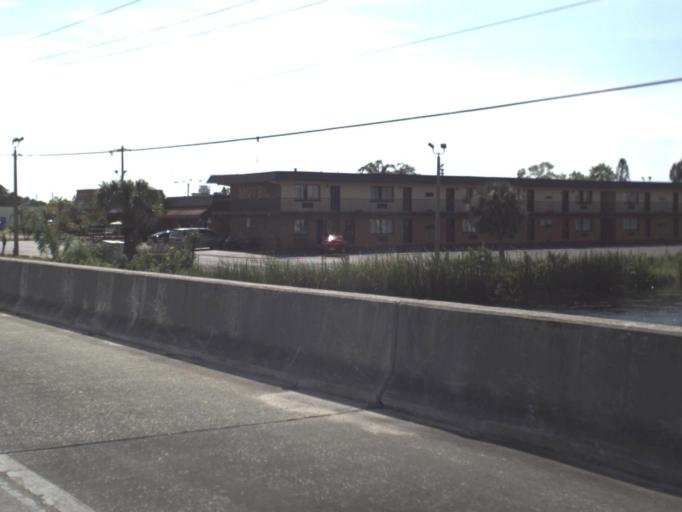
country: US
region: Florida
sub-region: Sarasota County
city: North Port
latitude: 27.0450
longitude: -82.2422
